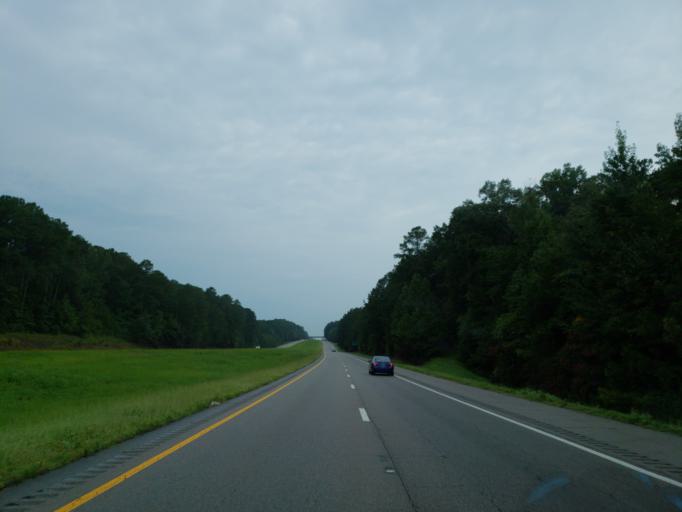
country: US
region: Mississippi
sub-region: Lauderdale County
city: Marion
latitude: 32.4028
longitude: -88.5574
